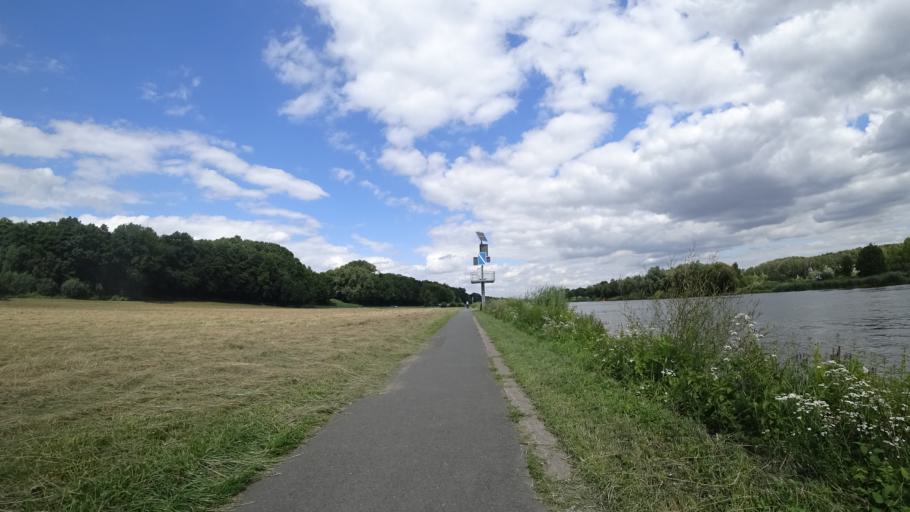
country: DE
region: North Rhine-Westphalia
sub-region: Regierungsbezirk Detmold
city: Petershagen
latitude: 52.3350
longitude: 8.9362
